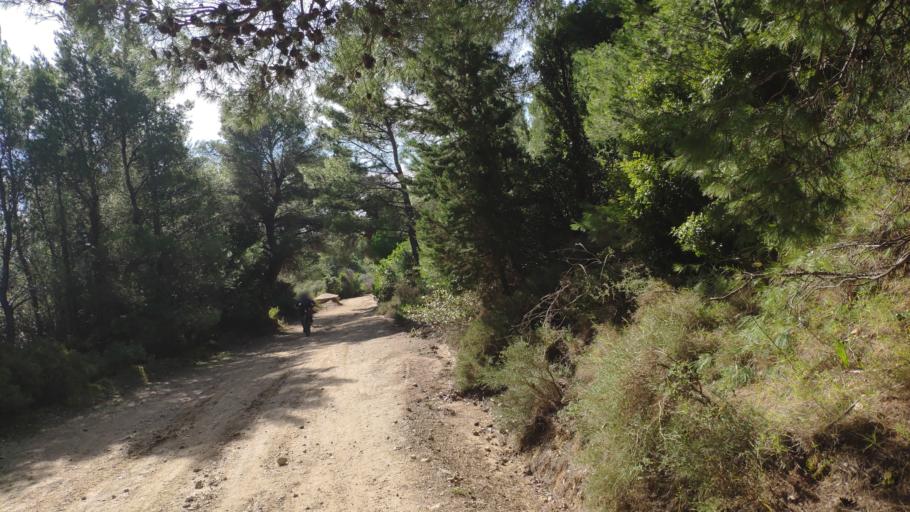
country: GR
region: Attica
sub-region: Nomarchia Anatolikis Attikis
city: Varybobi
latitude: 38.1565
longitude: 23.7769
